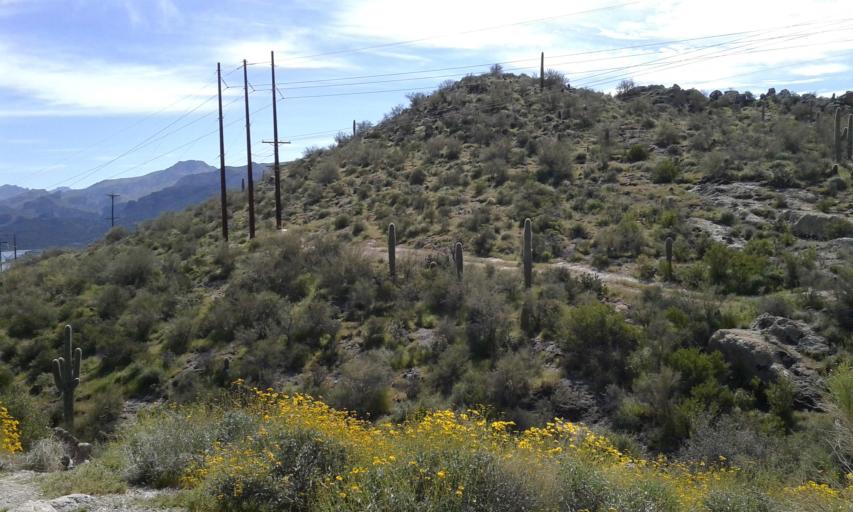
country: US
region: Arizona
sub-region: Pinal County
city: Apache Junction
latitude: 33.5410
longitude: -111.4491
